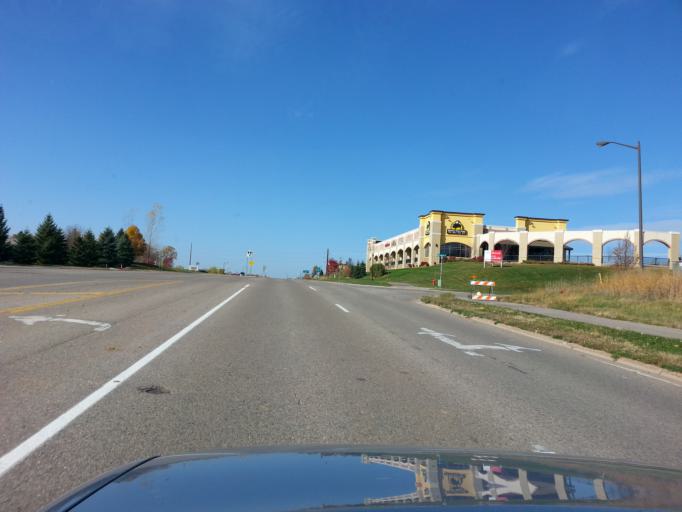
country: US
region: Minnesota
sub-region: Dakota County
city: Lakeville
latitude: 44.6814
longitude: -93.2847
